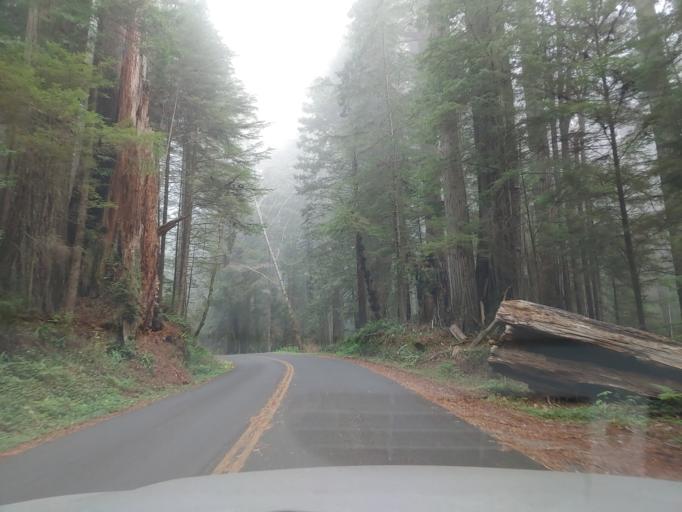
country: US
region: California
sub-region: Del Norte County
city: Bertsch-Oceanview
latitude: 41.4609
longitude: -124.0531
